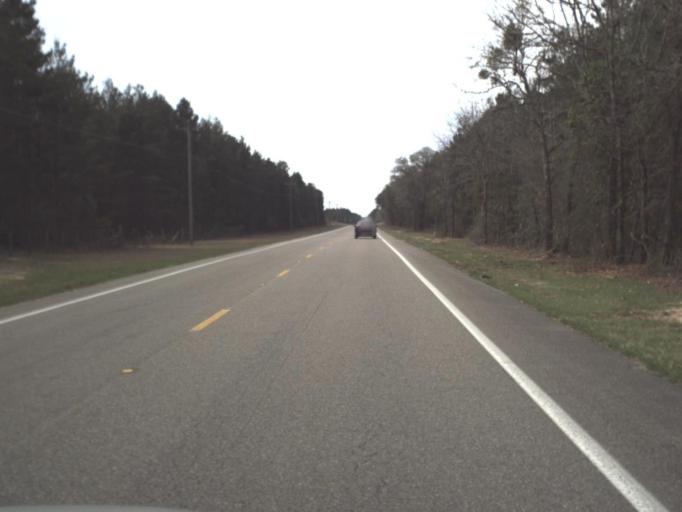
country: US
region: Florida
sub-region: Liberty County
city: Bristol
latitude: 30.4754
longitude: -84.9291
